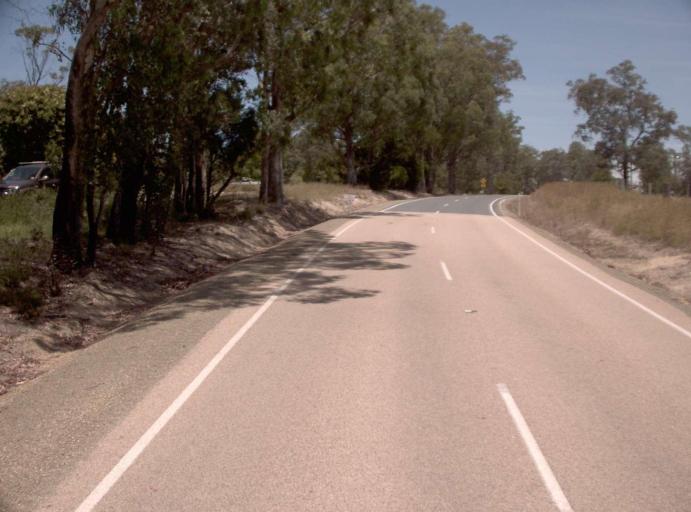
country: AU
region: Victoria
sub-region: East Gippsland
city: Lakes Entrance
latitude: -37.6831
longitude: 147.8447
